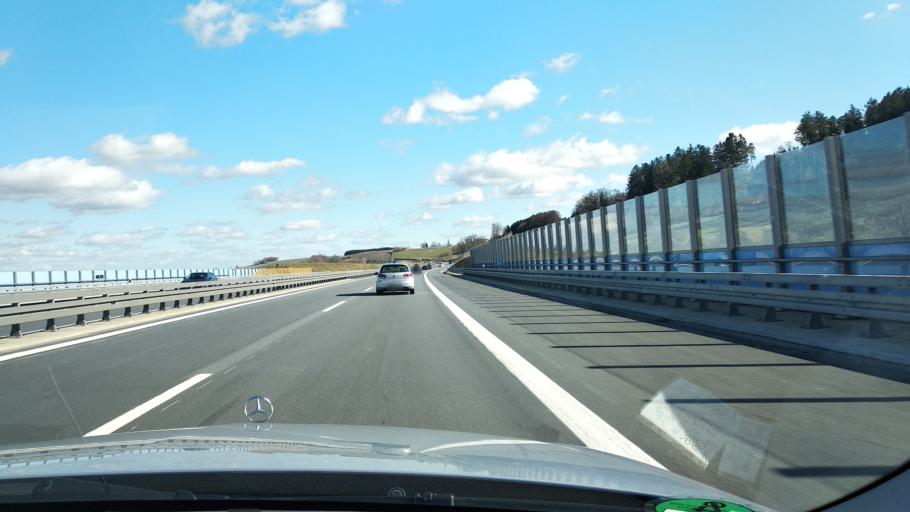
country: DE
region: Bavaria
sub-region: Upper Bavaria
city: Lengdorf
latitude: 48.2490
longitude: 12.0785
